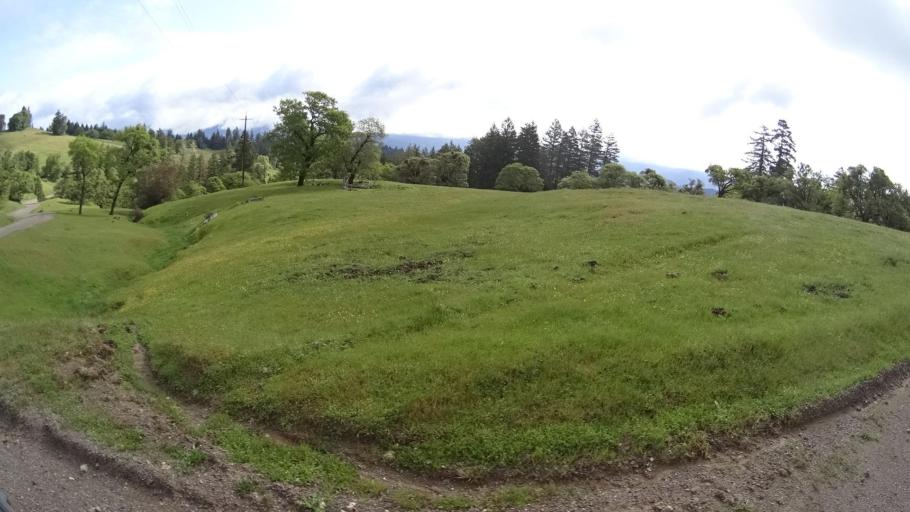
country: US
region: California
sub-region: Humboldt County
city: Redway
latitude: 40.2051
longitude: -123.6908
